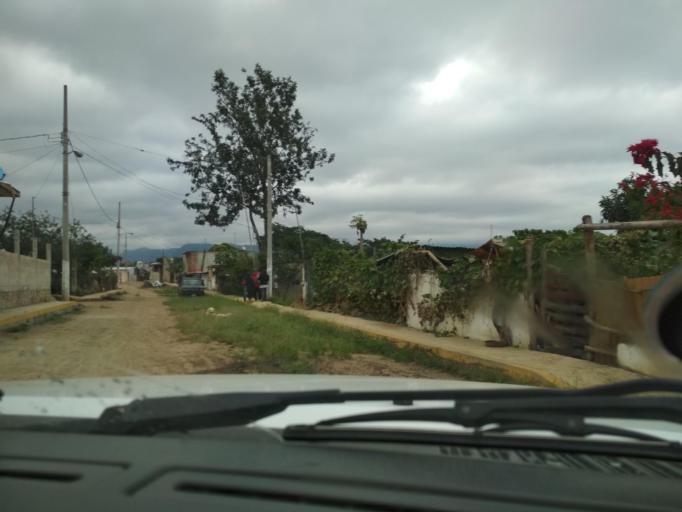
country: MX
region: Veracruz
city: El Castillo
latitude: 19.5718
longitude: -96.8488
